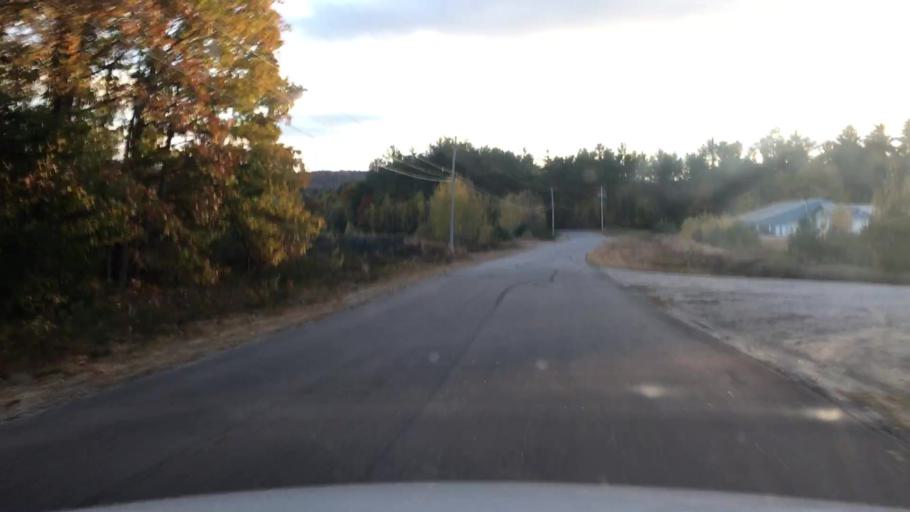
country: US
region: Maine
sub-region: Cumberland County
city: Harrison
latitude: 44.2428
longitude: -70.7411
